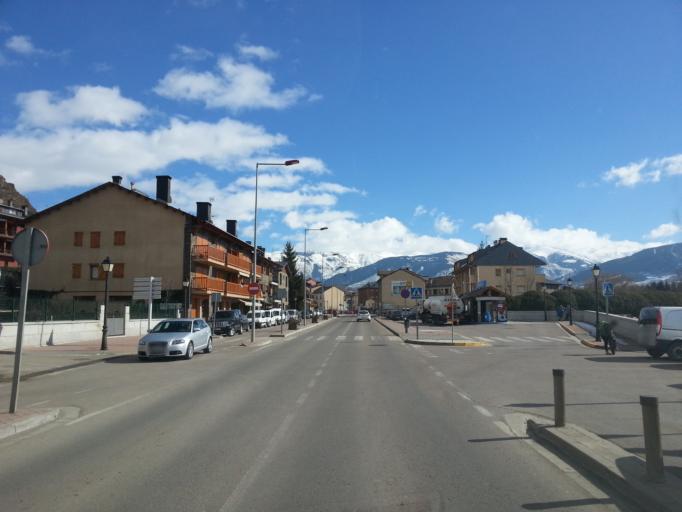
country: ES
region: Catalonia
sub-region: Provincia de Girona
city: Llivia
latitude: 42.4631
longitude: 1.9823
